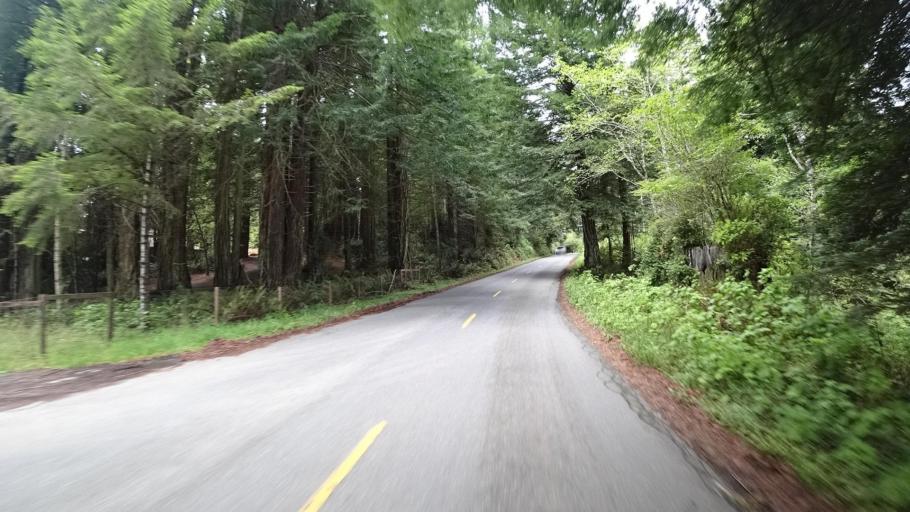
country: US
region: California
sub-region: Humboldt County
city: Bayside
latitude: 40.7977
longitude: -124.0465
